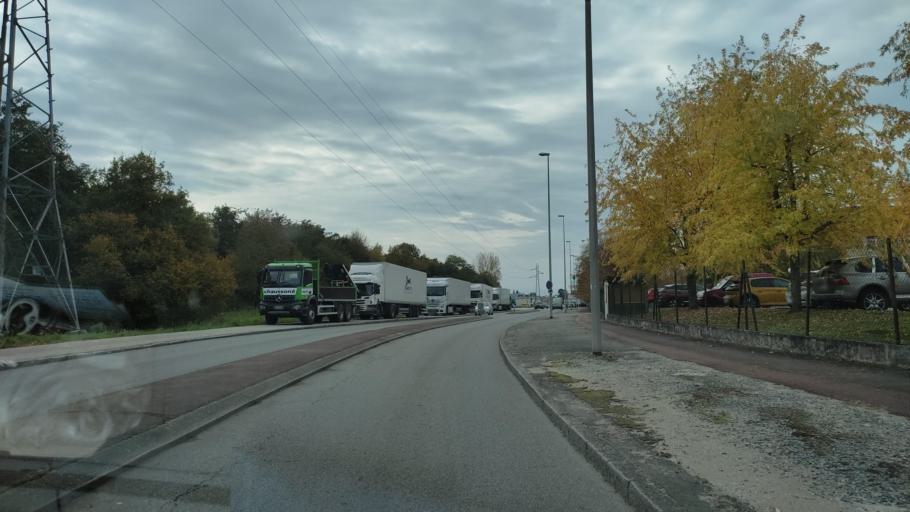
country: FR
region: Limousin
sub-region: Departement de la Haute-Vienne
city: Chaptelat
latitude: 45.8795
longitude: 1.2774
